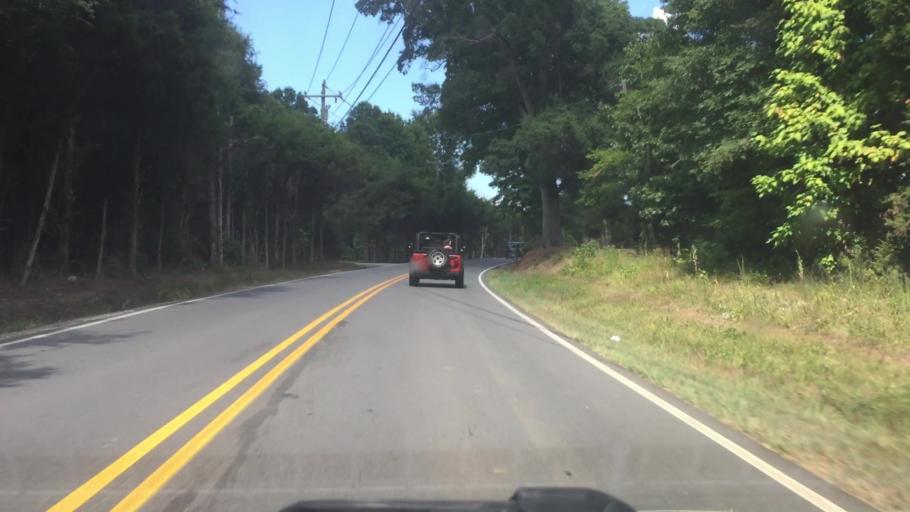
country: US
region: North Carolina
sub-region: Mecklenburg County
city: Huntersville
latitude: 35.4324
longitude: -80.7298
